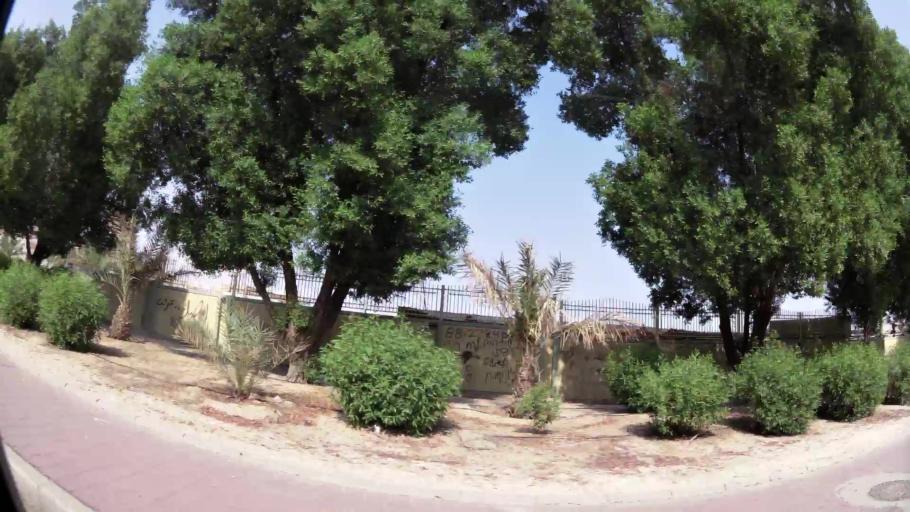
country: KW
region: Muhafazat al Jahra'
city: Al Jahra'
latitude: 29.3295
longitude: 47.6583
